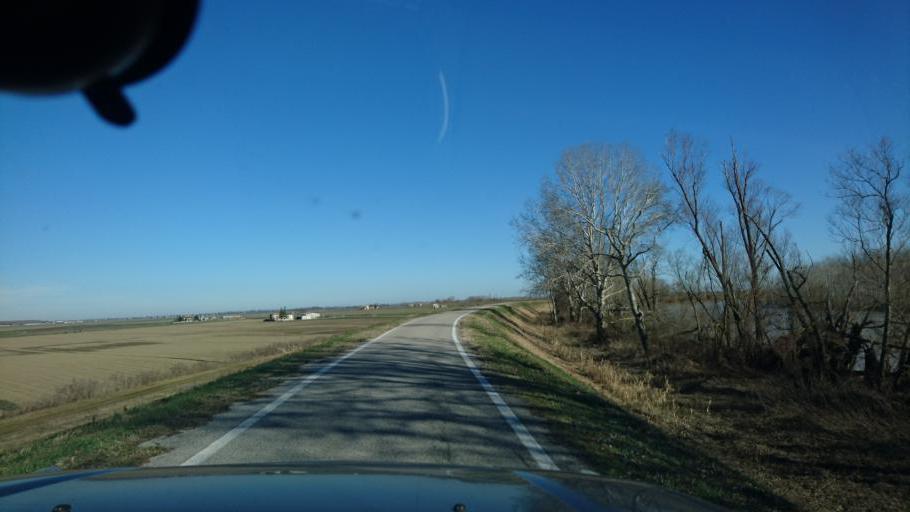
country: IT
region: Veneto
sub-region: Provincia di Rovigo
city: Ariano
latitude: 44.9304
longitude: 12.1463
